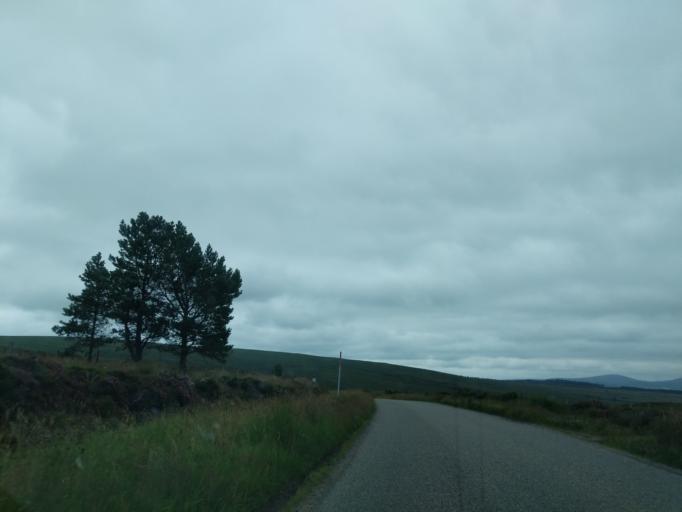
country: GB
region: Scotland
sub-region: Moray
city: Elgin
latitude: 57.5030
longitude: -3.4029
